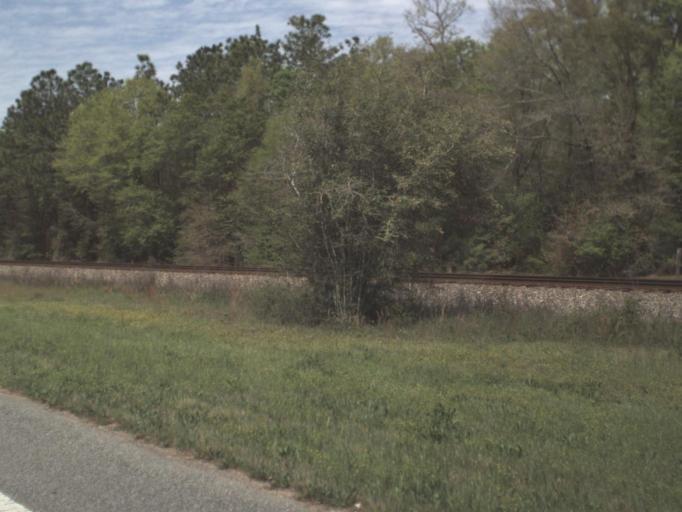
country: US
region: Florida
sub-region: Okaloosa County
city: Crestview
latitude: 30.7190
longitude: -86.7392
